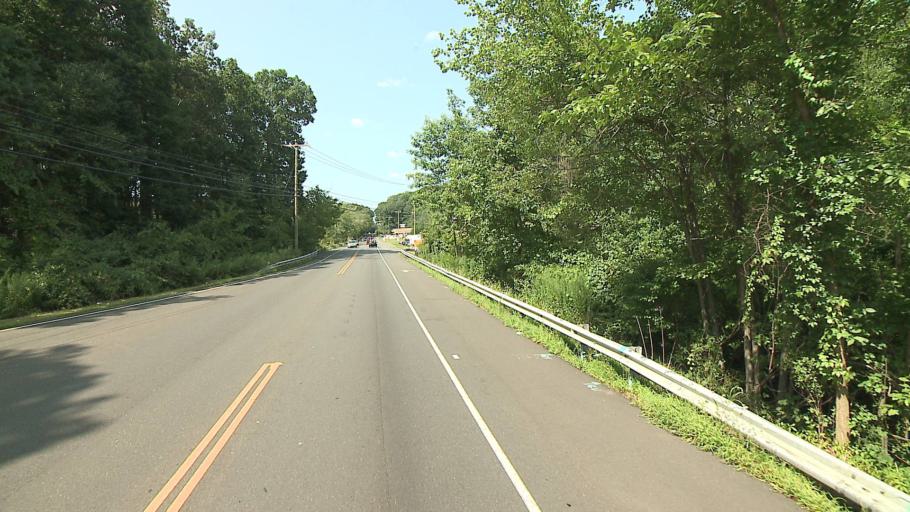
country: US
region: Connecticut
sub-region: Fairfield County
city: Trumbull
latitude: 41.3087
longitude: -73.2569
